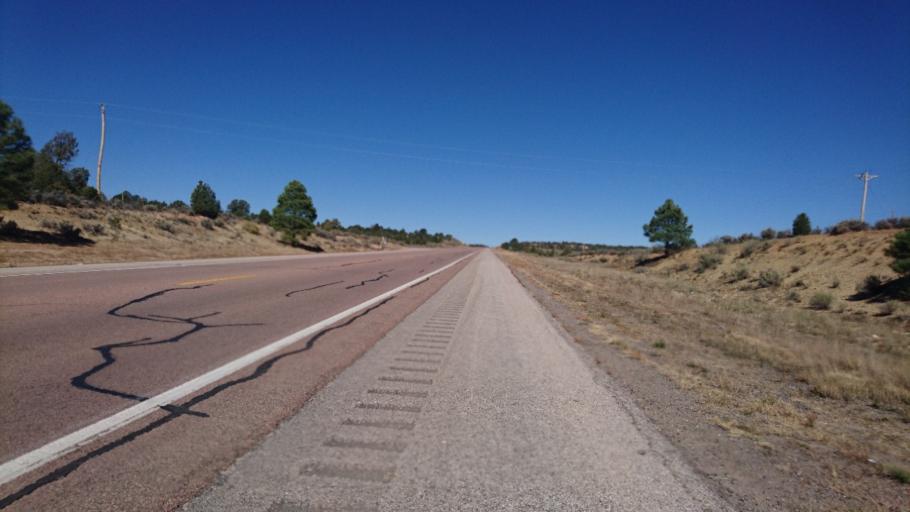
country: US
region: New Mexico
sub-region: McKinley County
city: Black Rock
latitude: 35.2947
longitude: -108.7567
